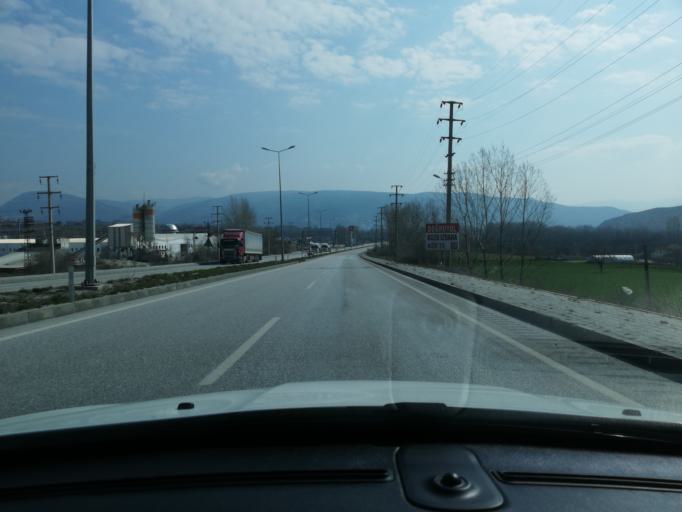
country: TR
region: Cankiri
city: Ilgaz
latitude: 40.9079
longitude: 33.6250
